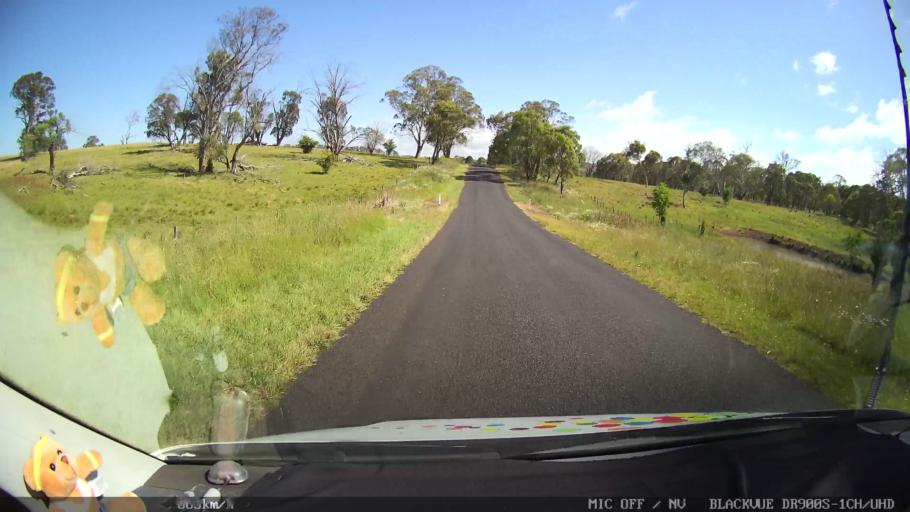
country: AU
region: New South Wales
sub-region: Guyra
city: Guyra
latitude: -30.1015
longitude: 151.6782
